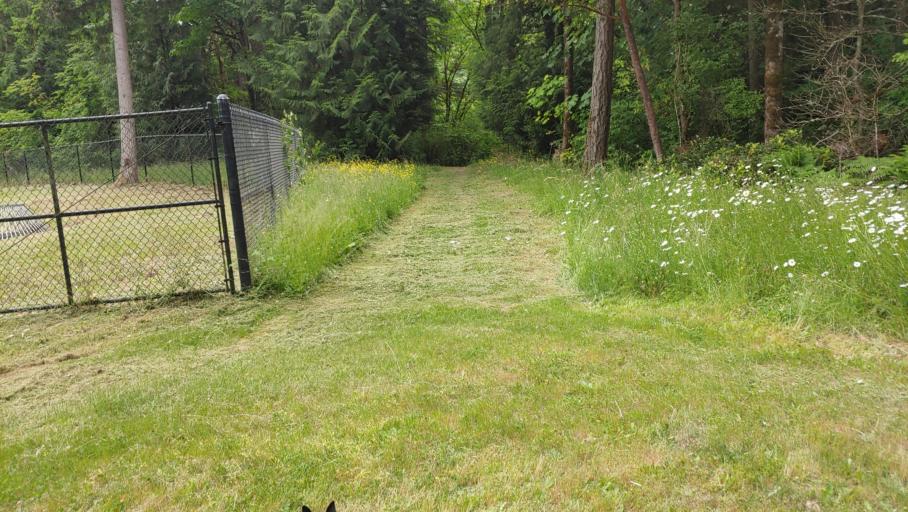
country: US
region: Washington
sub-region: King County
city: Newcastle
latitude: 47.5194
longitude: -122.1611
